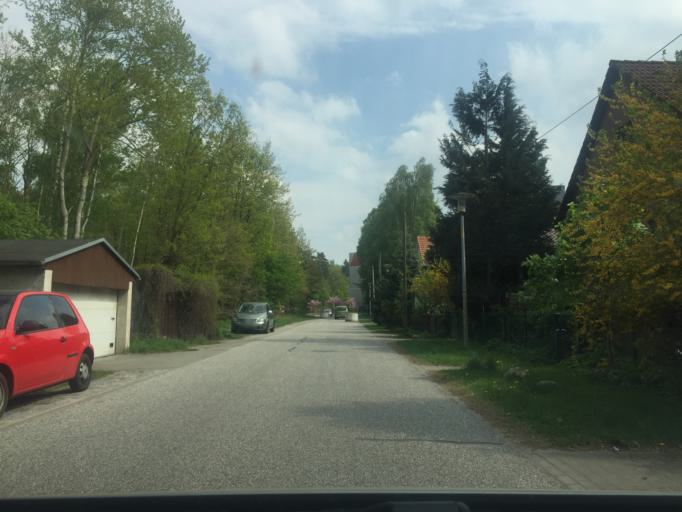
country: DE
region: Mecklenburg-Vorpommern
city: Torgelow
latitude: 53.6203
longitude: 14.0326
